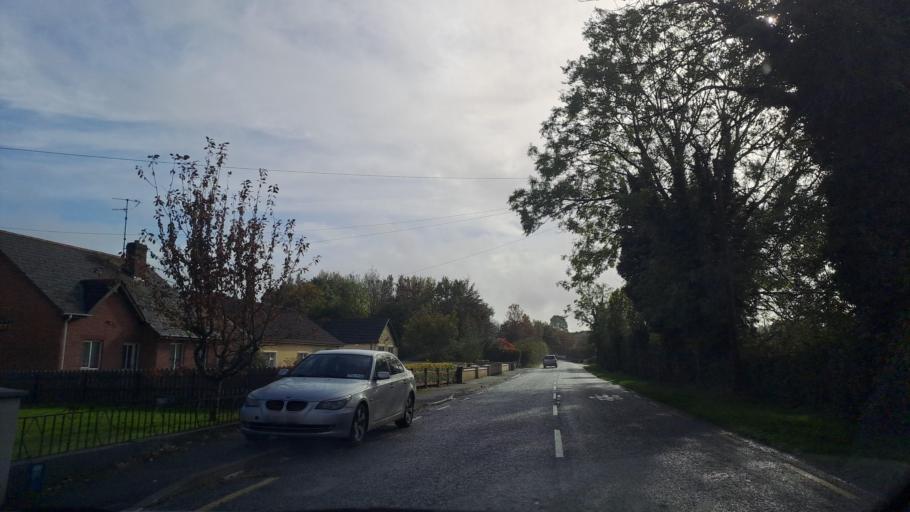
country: IE
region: Ulster
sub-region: County Monaghan
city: Carrickmacross
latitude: 53.9598
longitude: -6.7123
